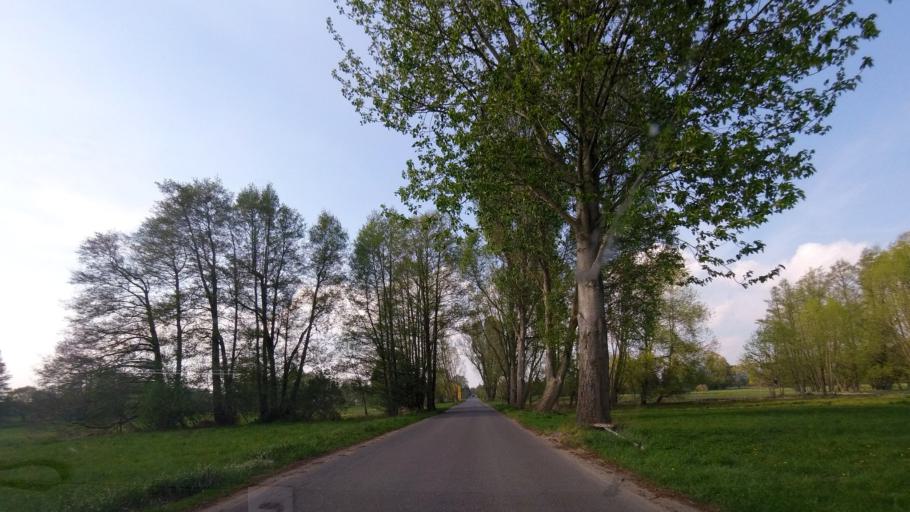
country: DE
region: Saxony-Anhalt
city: Zahna
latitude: 51.9152
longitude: 12.7945
